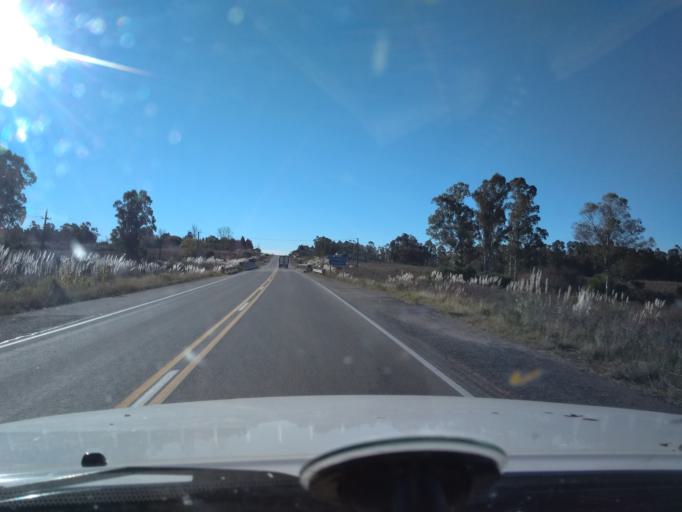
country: UY
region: Canelones
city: Sauce
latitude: -34.5952
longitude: -56.0515
